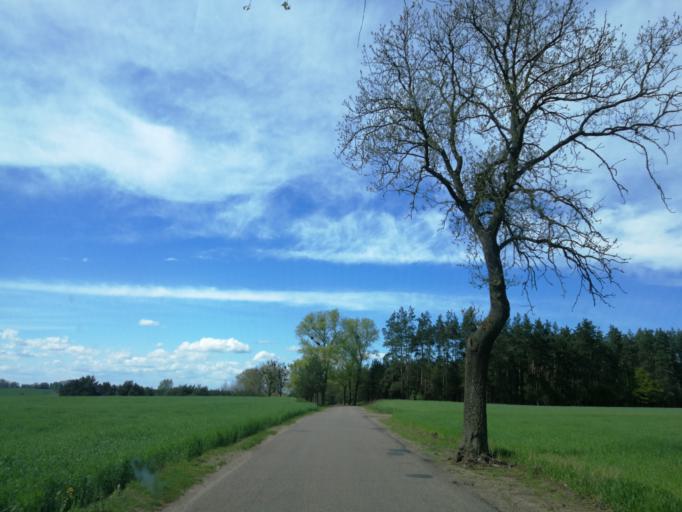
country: PL
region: Warmian-Masurian Voivodeship
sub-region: Powiat ilawski
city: Lubawa
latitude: 53.5916
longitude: 19.7255
